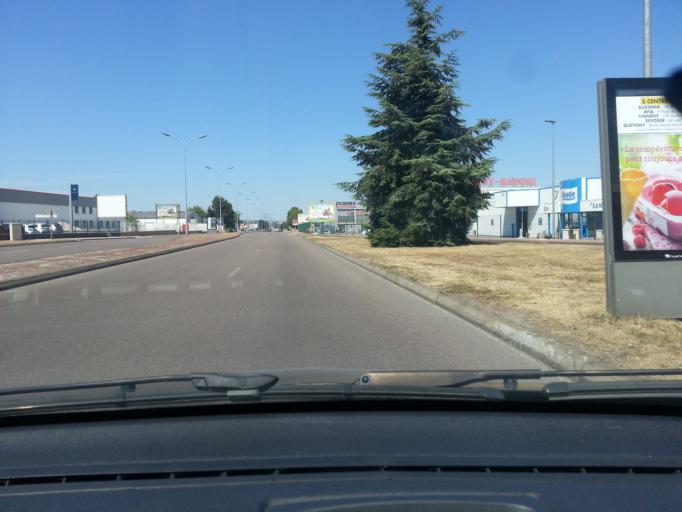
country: FR
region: Bourgogne
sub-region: Departement de la Cote-d'Or
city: Chenove
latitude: 47.2911
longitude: 5.0208
